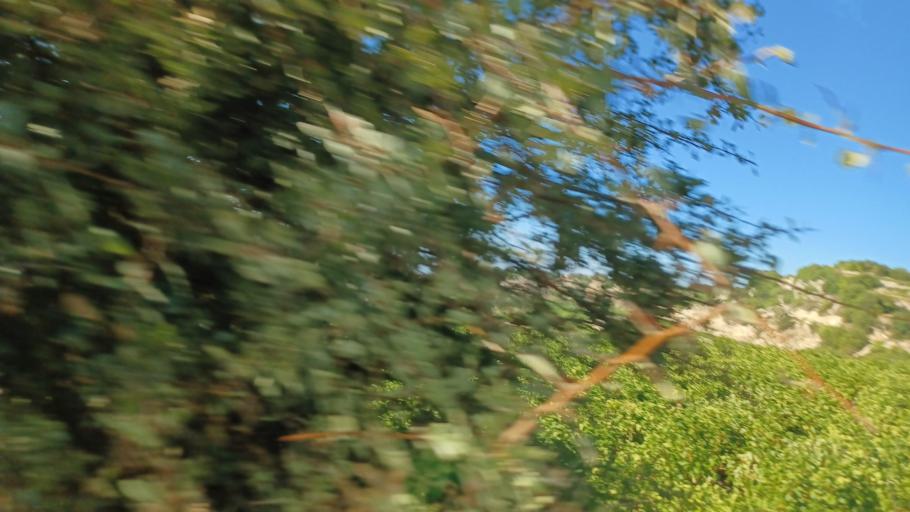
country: CY
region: Pafos
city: Mesogi
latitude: 34.8961
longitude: 32.6287
